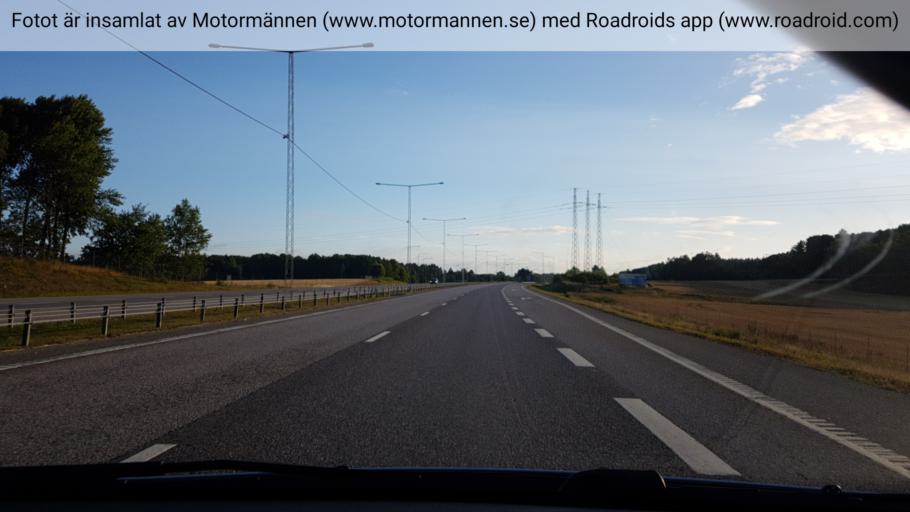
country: SE
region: Stockholm
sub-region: Haninge Kommun
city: Jordbro
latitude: 59.1175
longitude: 18.1287
